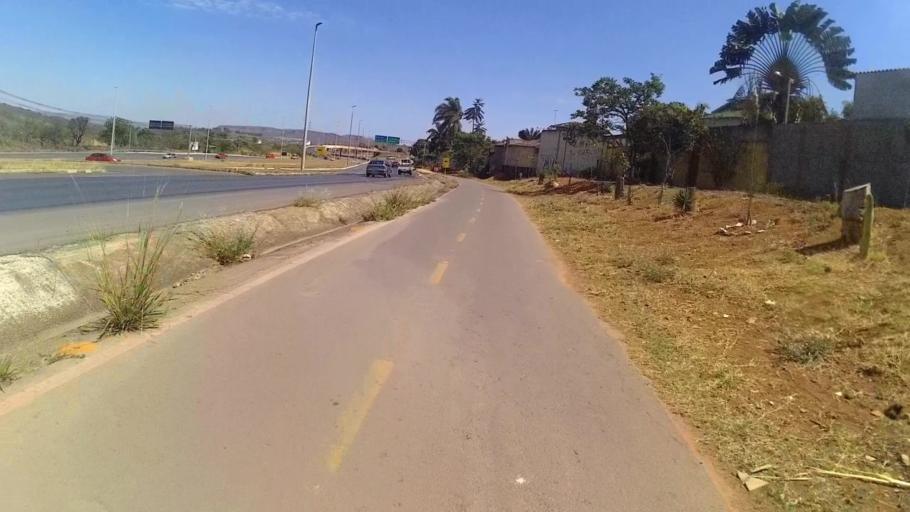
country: BR
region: Federal District
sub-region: Brasilia
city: Brasilia
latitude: -15.6453
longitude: -47.8472
